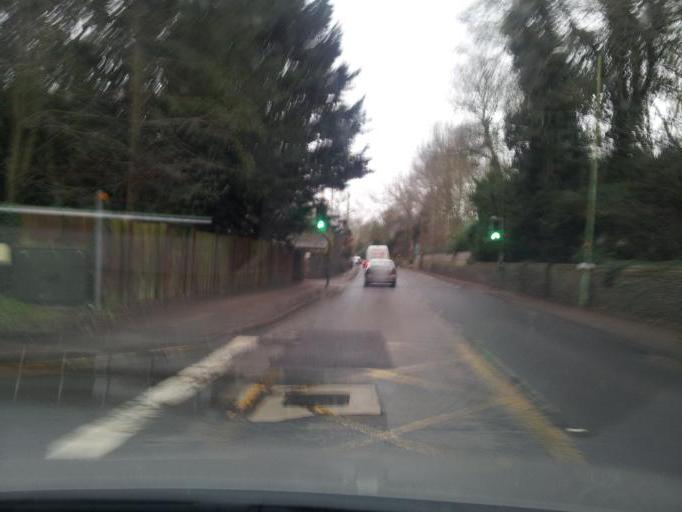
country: GB
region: England
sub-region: Suffolk
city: Great Barton
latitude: 52.2686
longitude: 0.7708
